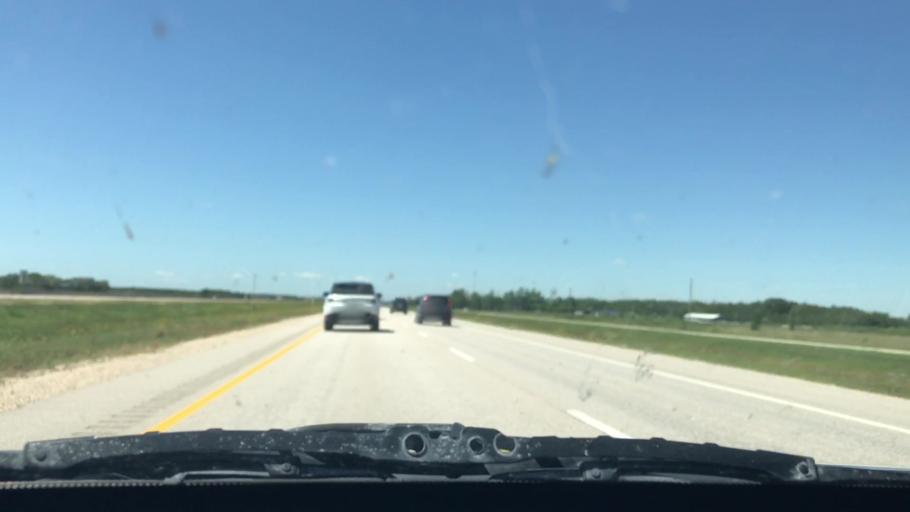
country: CA
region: Manitoba
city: Winnipeg
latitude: 49.8125
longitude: -96.9166
